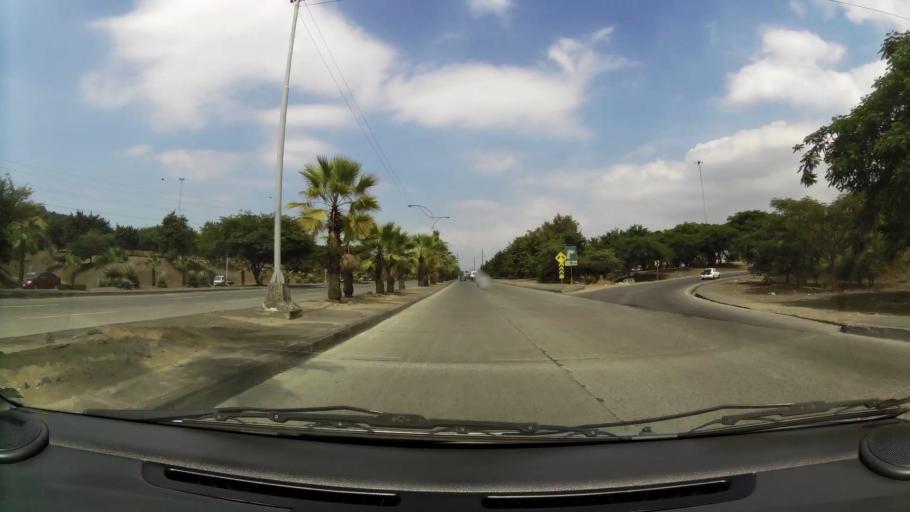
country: EC
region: Guayas
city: Eloy Alfaro
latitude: -2.0753
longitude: -79.9191
